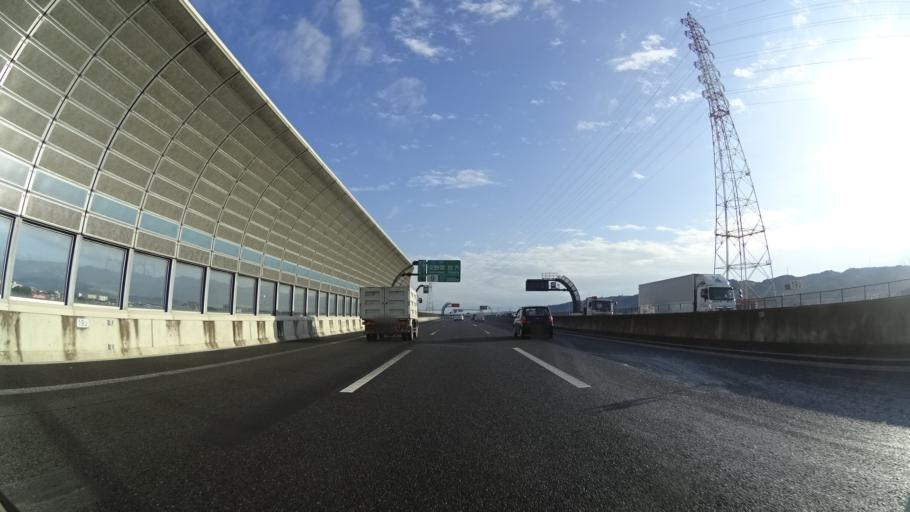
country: JP
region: Osaka
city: Neyagawa
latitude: 34.7719
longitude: 135.6603
